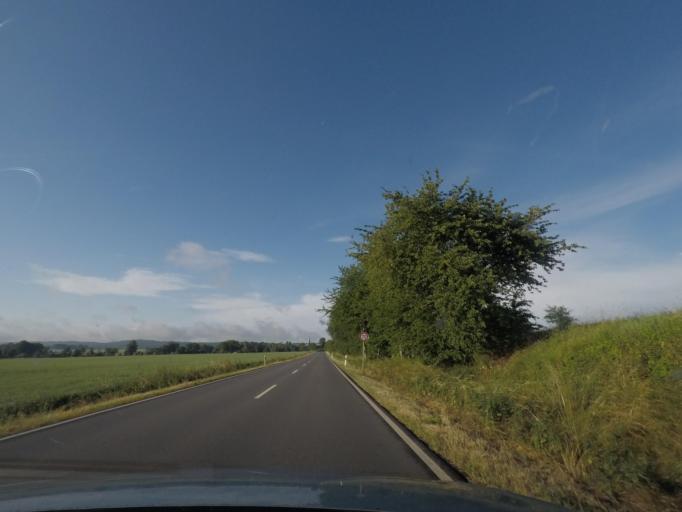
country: DE
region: Saxony-Anhalt
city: Huy-Neinstedt
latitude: 51.9943
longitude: 10.8939
